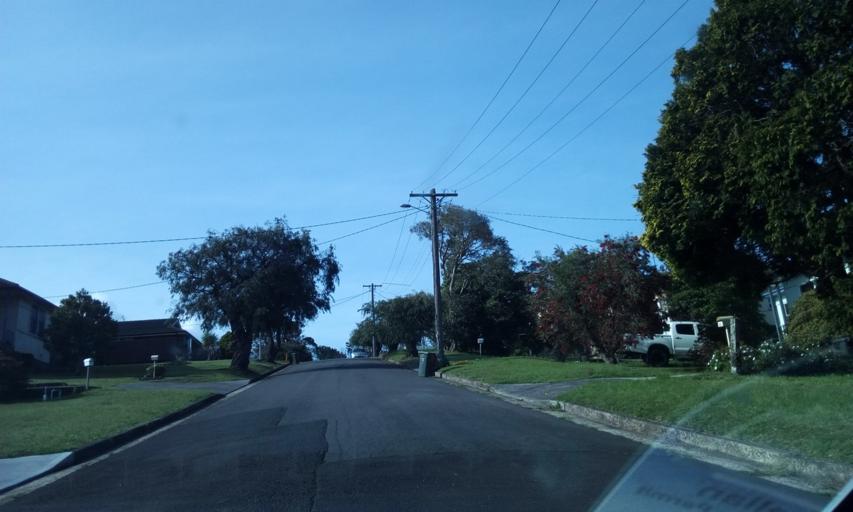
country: AU
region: New South Wales
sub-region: Wollongong
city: Mount Saint Thomas
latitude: -34.4425
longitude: 150.8687
